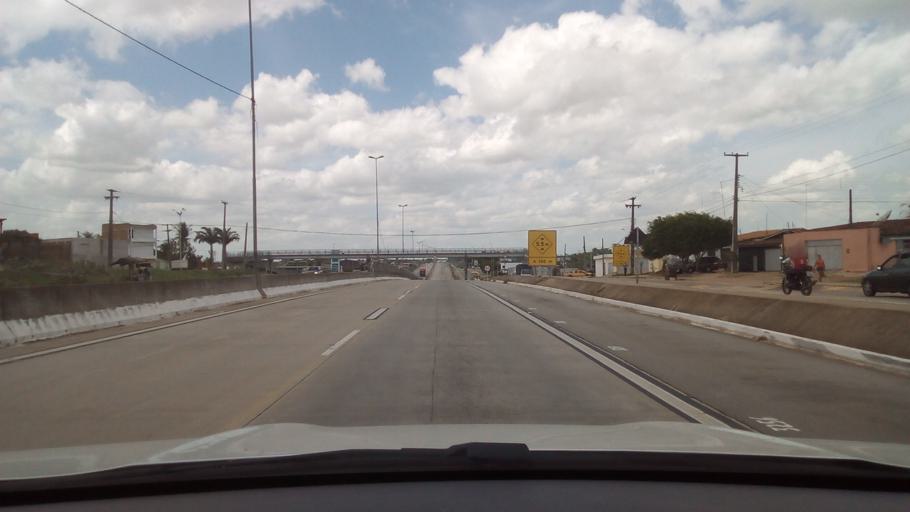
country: BR
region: Paraiba
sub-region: Mamanguape
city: Mamanguape
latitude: -6.8459
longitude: -35.1356
